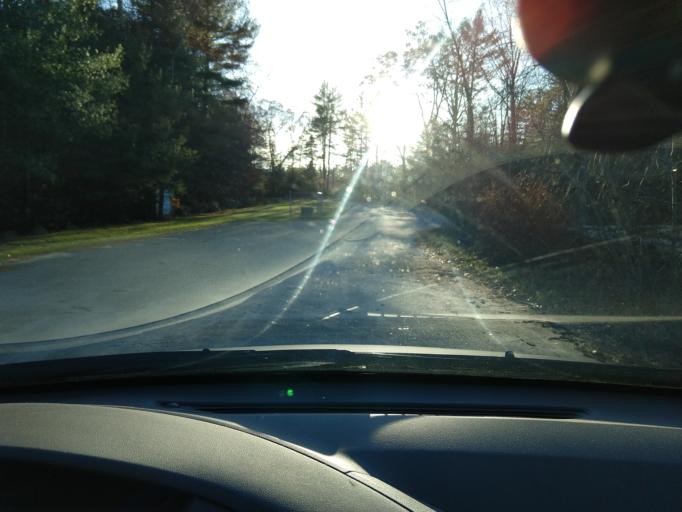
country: US
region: Massachusetts
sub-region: Middlesex County
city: Carlisle
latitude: 42.5238
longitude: -71.3416
